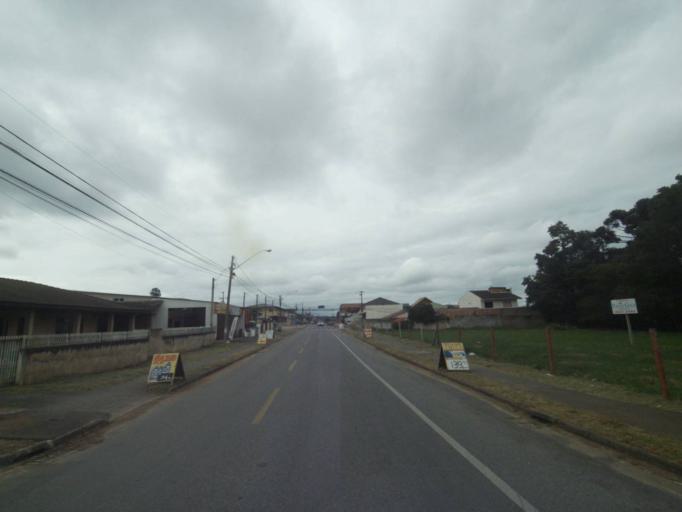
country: BR
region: Parana
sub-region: Quatro Barras
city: Quatro Barras
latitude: -25.3588
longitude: -49.1096
